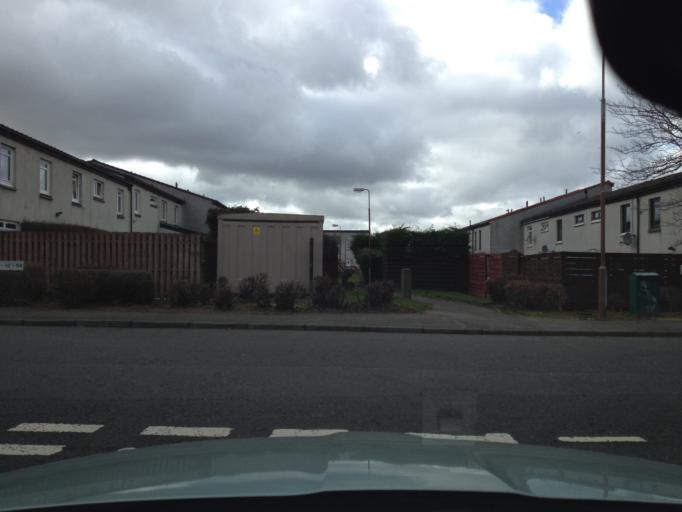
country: GB
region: Scotland
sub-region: West Lothian
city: Livingston
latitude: 55.8759
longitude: -3.5211
